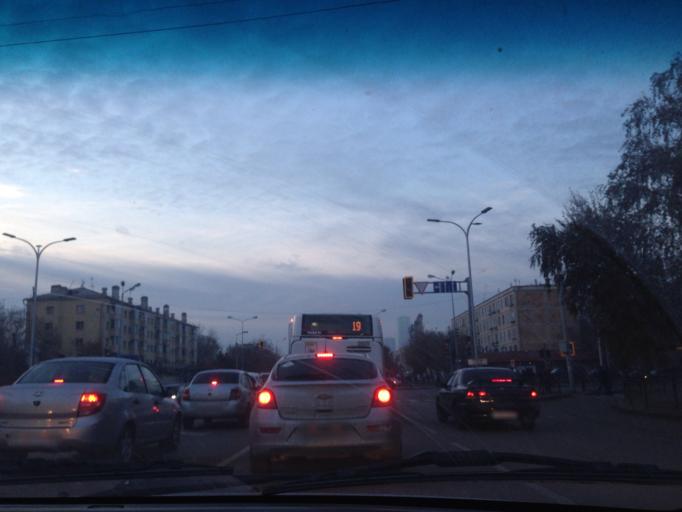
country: KZ
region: Astana Qalasy
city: Astana
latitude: 51.1771
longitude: 71.4182
